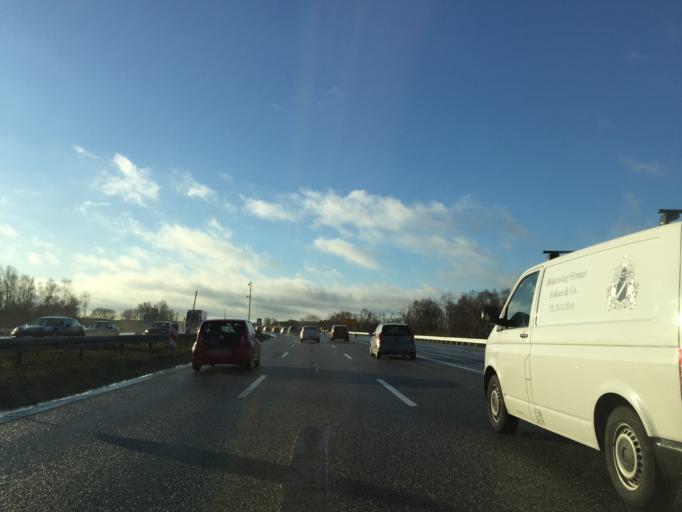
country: DK
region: Zealand
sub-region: Solrod Kommune
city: Solrod
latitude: 55.5137
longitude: 12.1837
